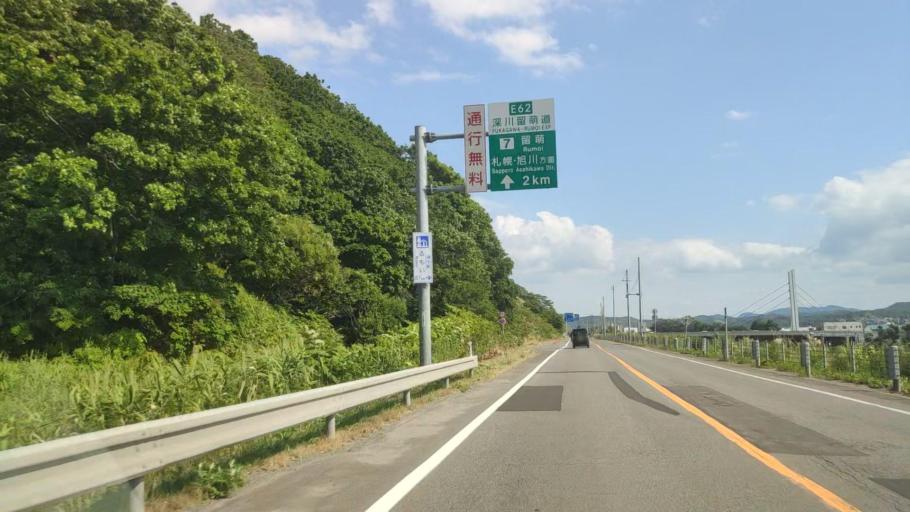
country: JP
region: Hokkaido
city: Rumoi
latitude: 43.9497
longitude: 141.6482
